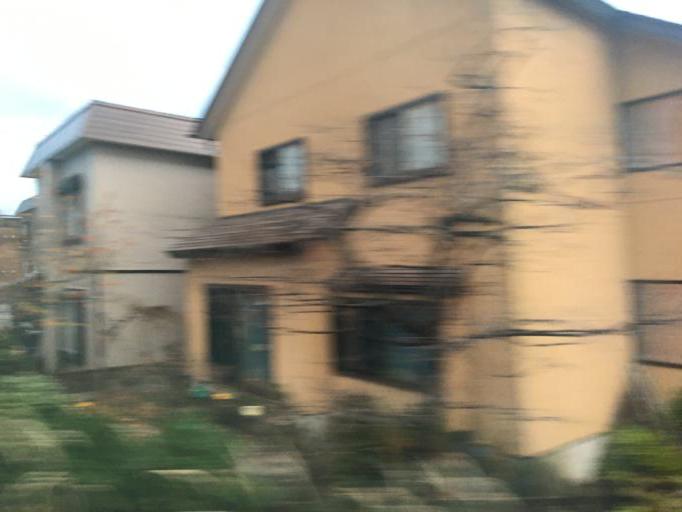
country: JP
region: Aomori
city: Aomori Shi
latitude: 40.8248
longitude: 140.7223
